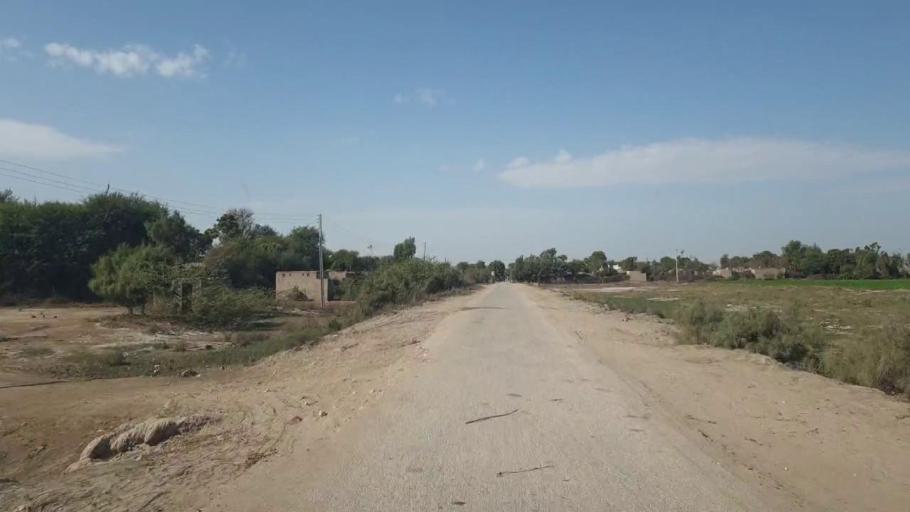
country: PK
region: Sindh
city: Hala
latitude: 25.9718
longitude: 68.3478
